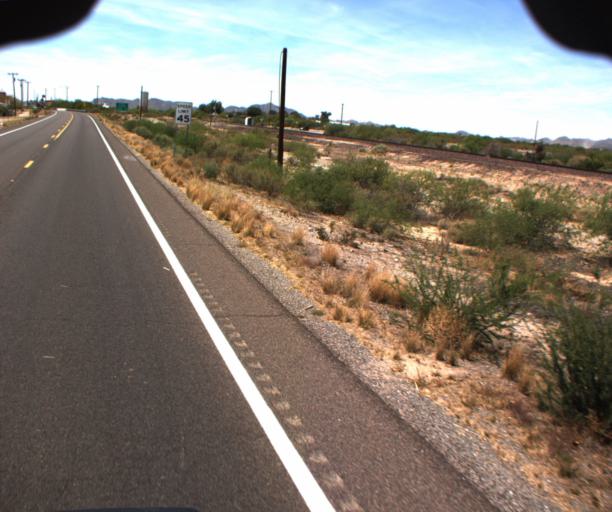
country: US
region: Arizona
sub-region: La Paz County
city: Salome
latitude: 33.7845
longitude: -113.6098
